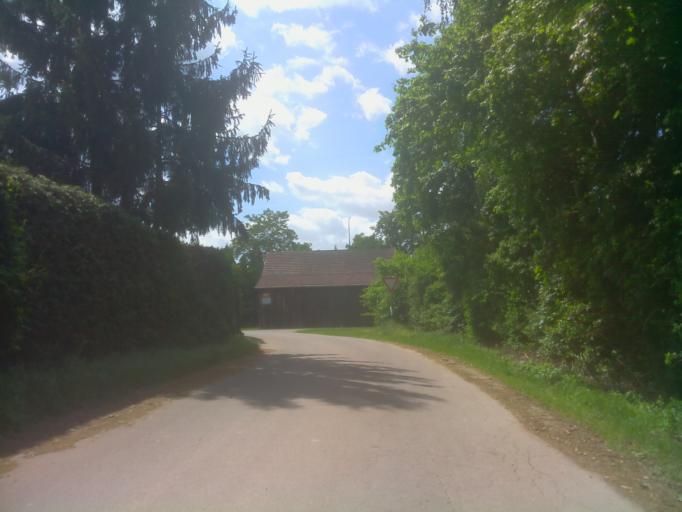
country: DE
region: Rheinland-Pfalz
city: Otterstadt
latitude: 49.3767
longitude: 8.4483
